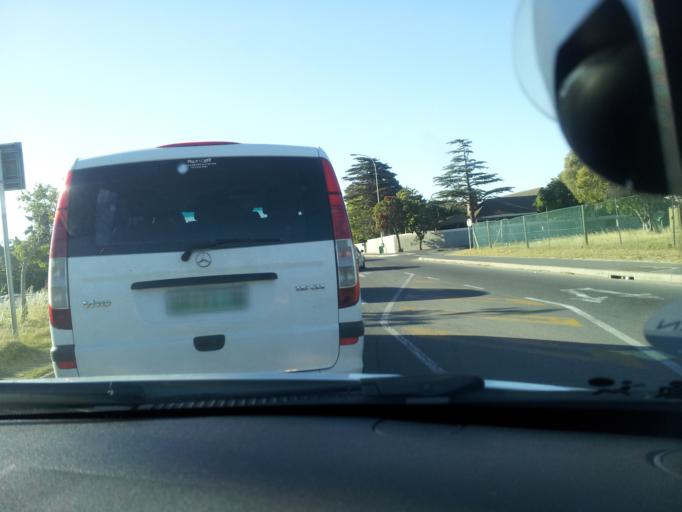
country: ZA
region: Western Cape
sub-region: Cape Winelands District Municipality
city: Stellenbosch
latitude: -34.1058
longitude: 18.8363
